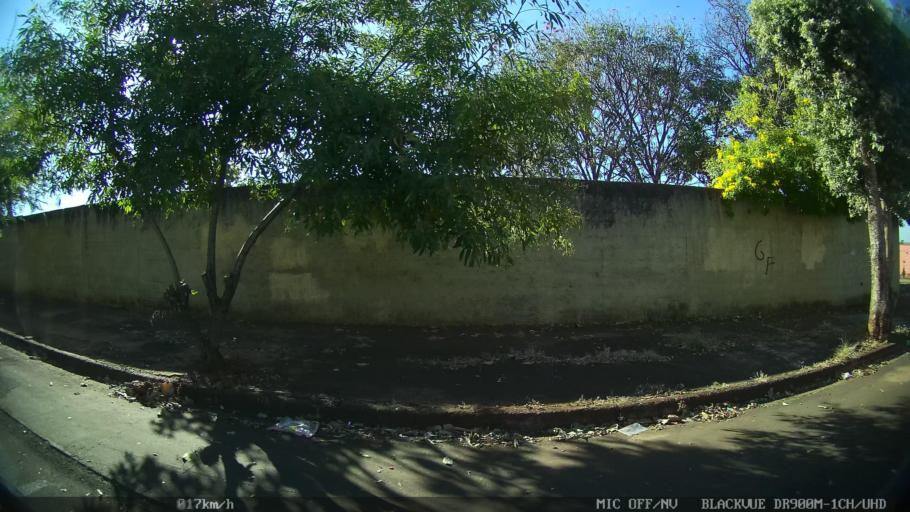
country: BR
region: Sao Paulo
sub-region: Olimpia
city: Olimpia
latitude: -20.7423
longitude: -48.8885
